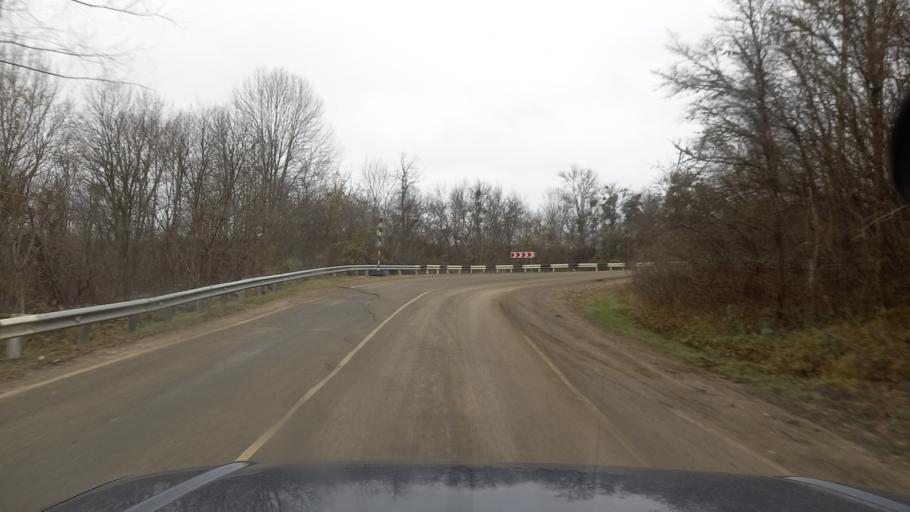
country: RU
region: Krasnodarskiy
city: Goryachiy Klyuch
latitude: 44.5551
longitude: 39.2514
